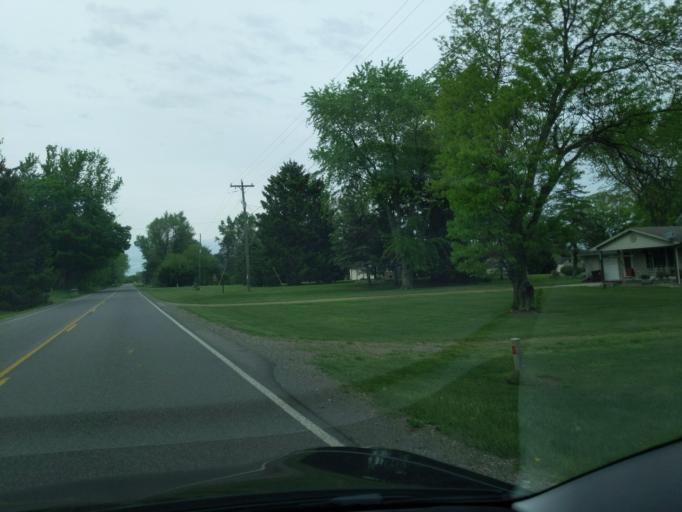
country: US
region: Michigan
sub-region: Ingham County
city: Leslie
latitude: 42.5039
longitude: -84.4268
